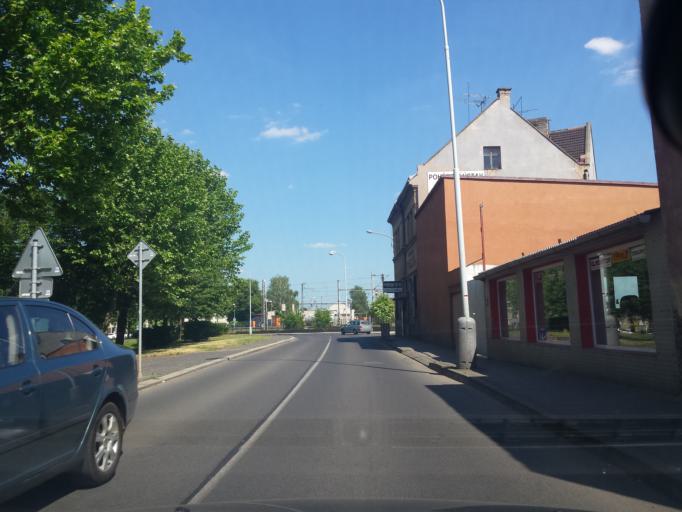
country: CZ
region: Central Bohemia
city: Kralupy nad Vltavou
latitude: 50.2384
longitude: 14.3069
